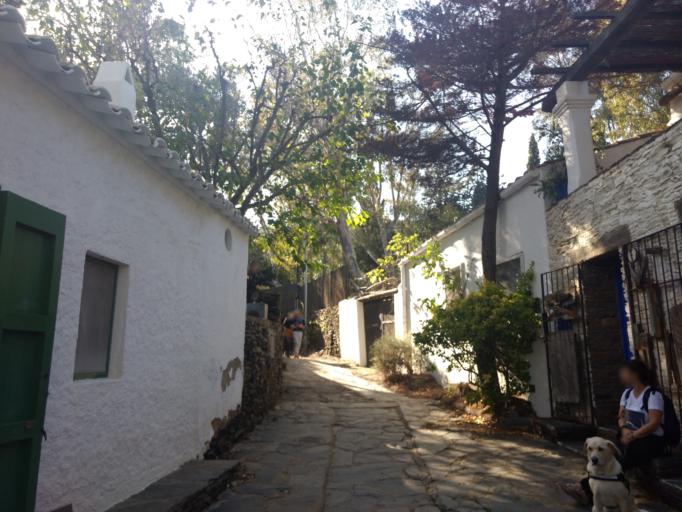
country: ES
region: Catalonia
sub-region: Provincia de Girona
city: Cadaques
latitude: 42.2933
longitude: 3.2858
